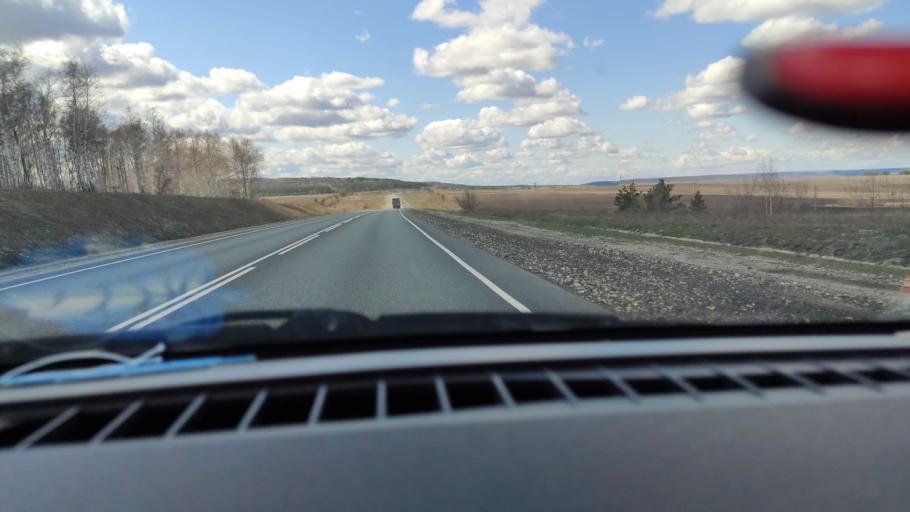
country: RU
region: Saratov
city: Khvalynsk
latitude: 52.5523
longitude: 48.0766
